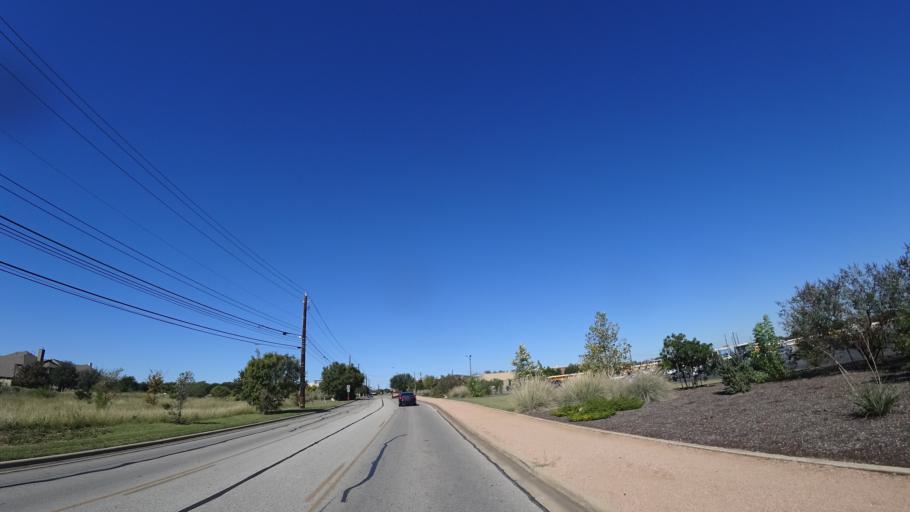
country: US
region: Texas
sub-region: Travis County
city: Rollingwood
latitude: 30.2297
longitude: -97.8120
